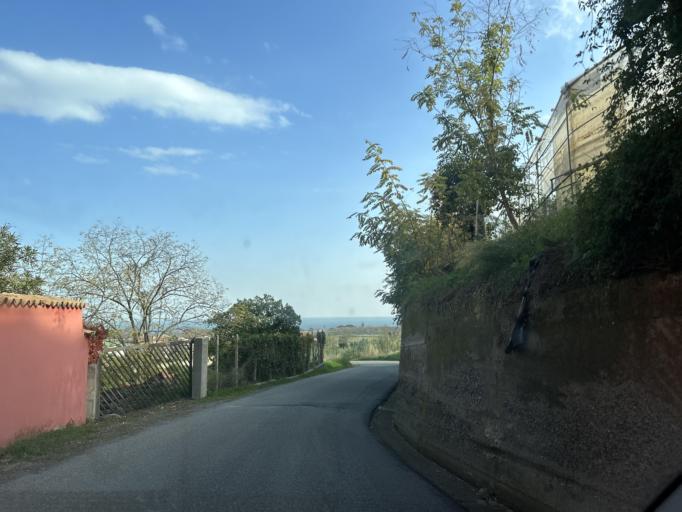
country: IT
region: Calabria
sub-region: Provincia di Catanzaro
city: Montepaone
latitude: 38.7163
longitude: 16.5205
